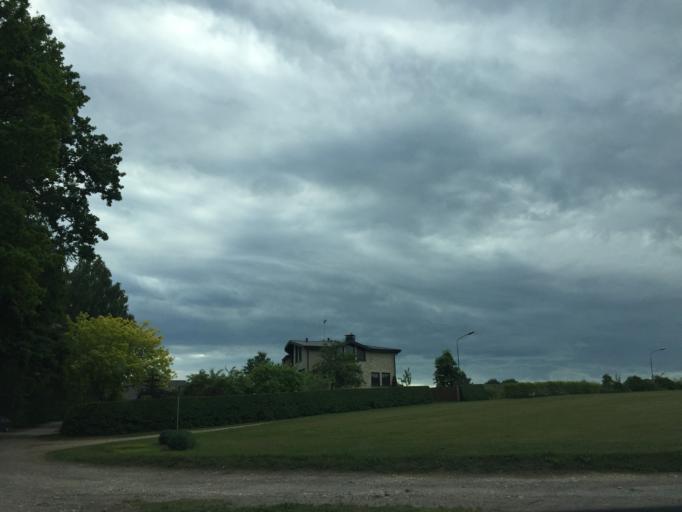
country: LV
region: Pargaujas
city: Stalbe
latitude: 57.3591
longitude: 24.9573
